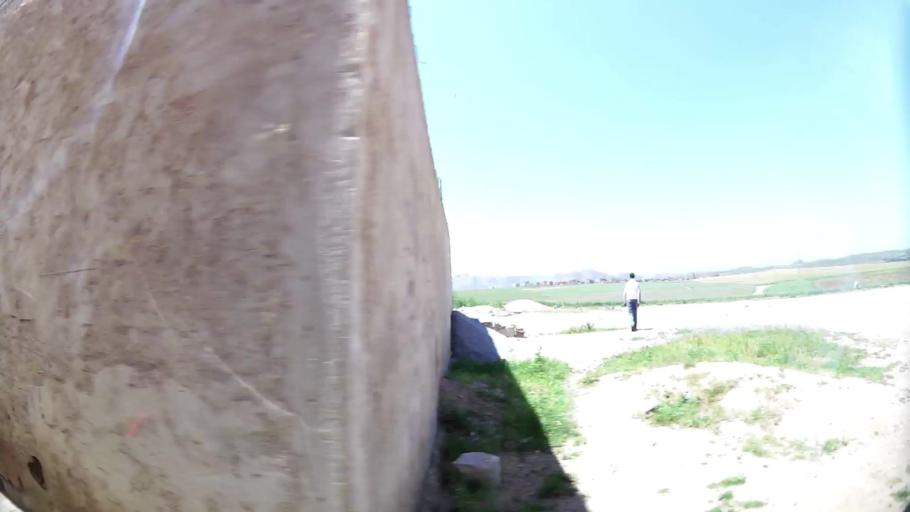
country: MA
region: Oriental
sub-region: Oujda-Angad
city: Oujda
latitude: 34.6872
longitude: -1.9551
